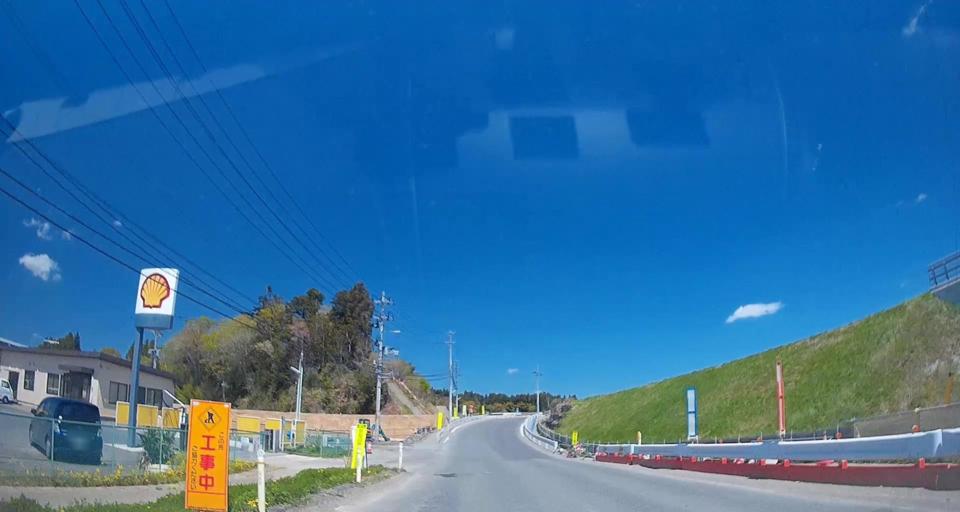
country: JP
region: Iwate
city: Ofunato
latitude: 38.8707
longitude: 141.5824
